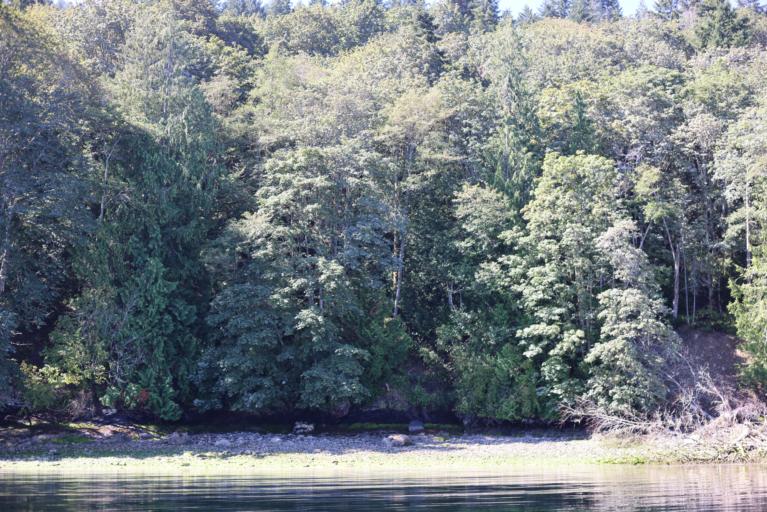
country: CA
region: British Columbia
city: North Cowichan
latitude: 48.8531
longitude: -123.6077
